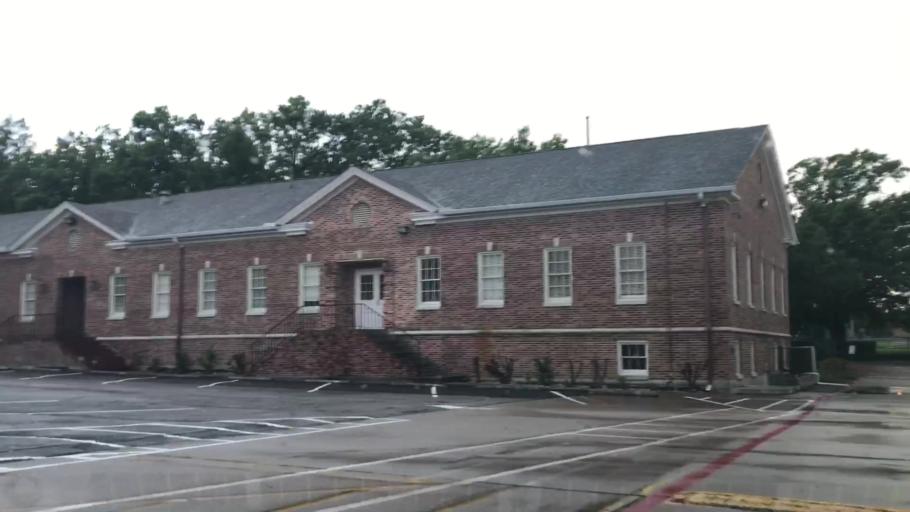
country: US
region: Texas
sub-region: Dallas County
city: University Park
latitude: 32.8957
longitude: -96.7893
